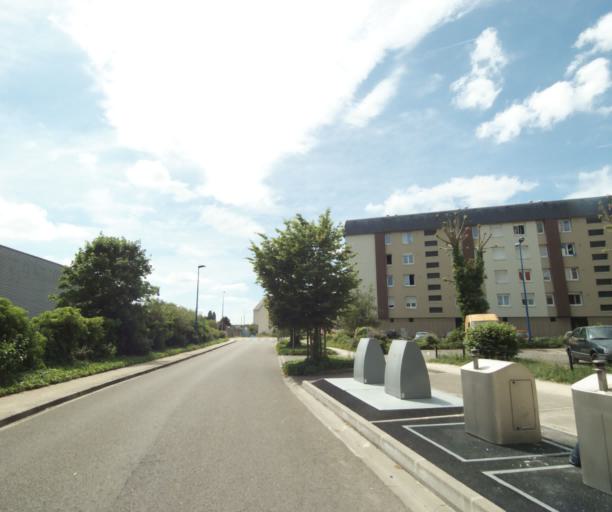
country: FR
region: Centre
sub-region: Departement d'Eure-et-Loir
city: Luce
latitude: 48.4335
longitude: 1.4618
